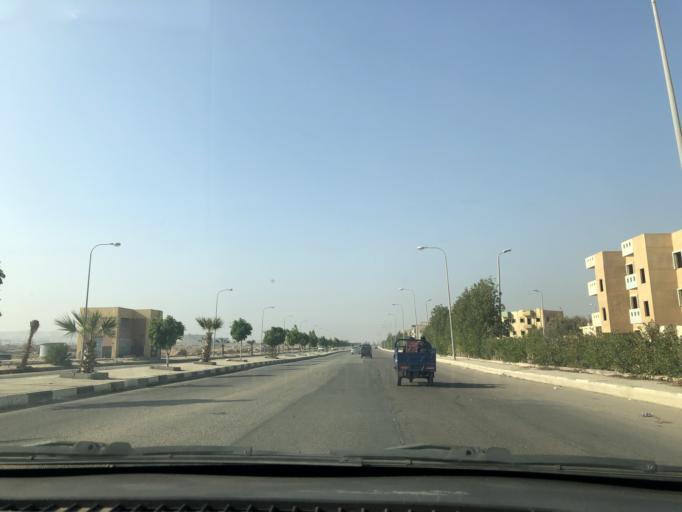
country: EG
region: Al Jizah
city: Madinat Sittah Uktubar
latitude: 29.9290
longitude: 31.0491
